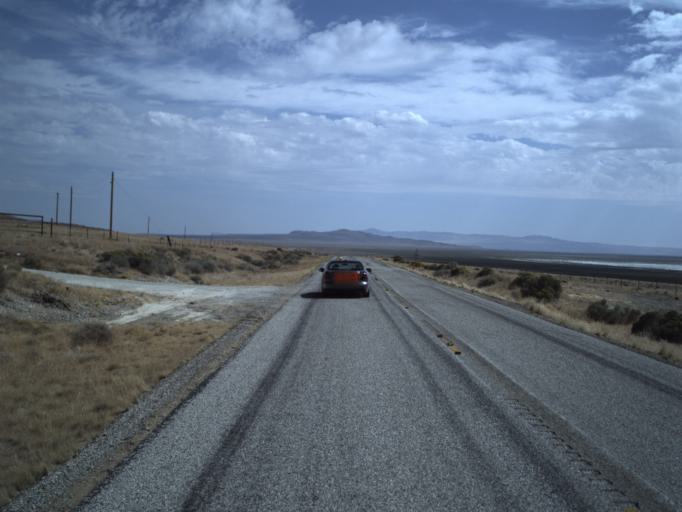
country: US
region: Utah
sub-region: Tooele County
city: Wendover
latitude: 41.4405
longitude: -113.7079
